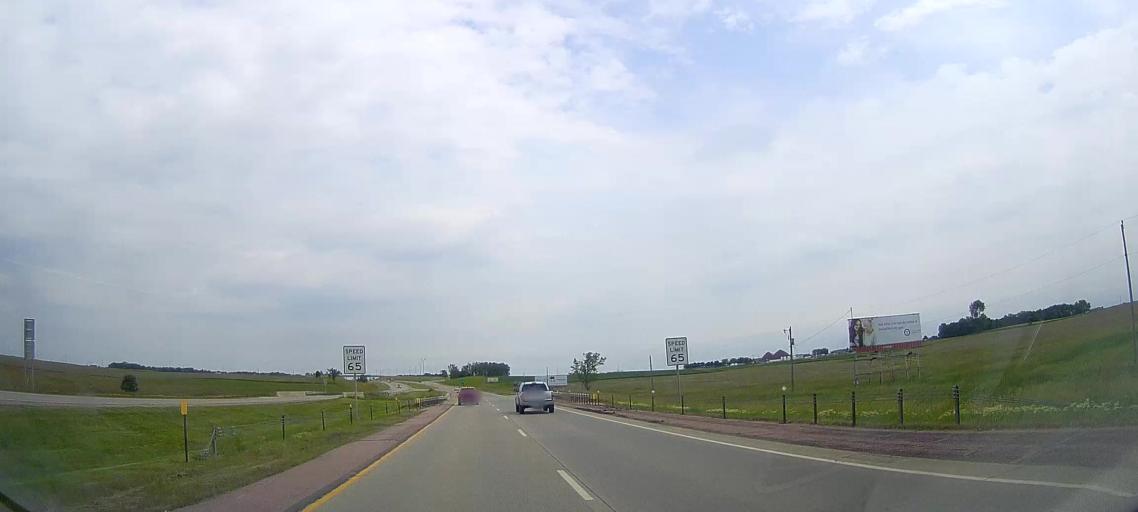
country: US
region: South Dakota
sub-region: Minnehaha County
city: Crooks
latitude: 43.6088
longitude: -96.8064
